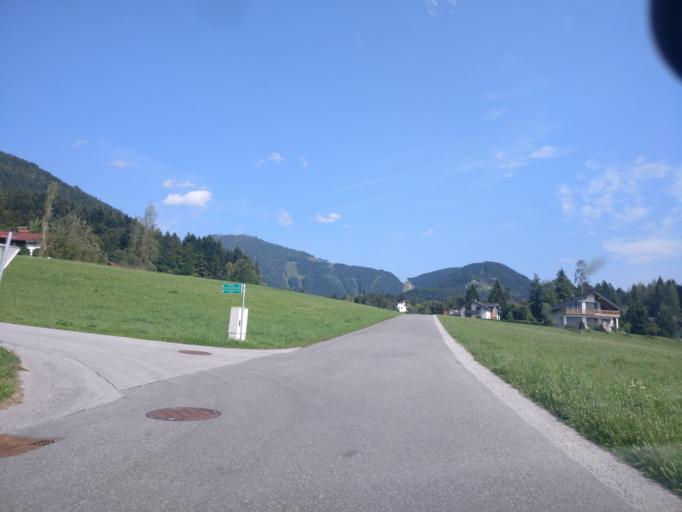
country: AT
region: Salzburg
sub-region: Politischer Bezirk Sankt Johann im Pongau
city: Werfenweng
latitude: 47.4642
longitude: 13.2291
